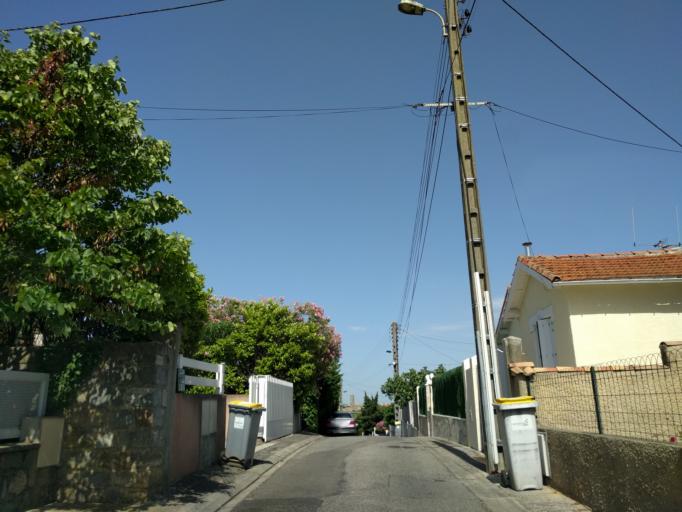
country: FR
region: Languedoc-Roussillon
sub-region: Departement de l'Aude
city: Carcassonne
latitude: 43.2105
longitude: 2.3678
